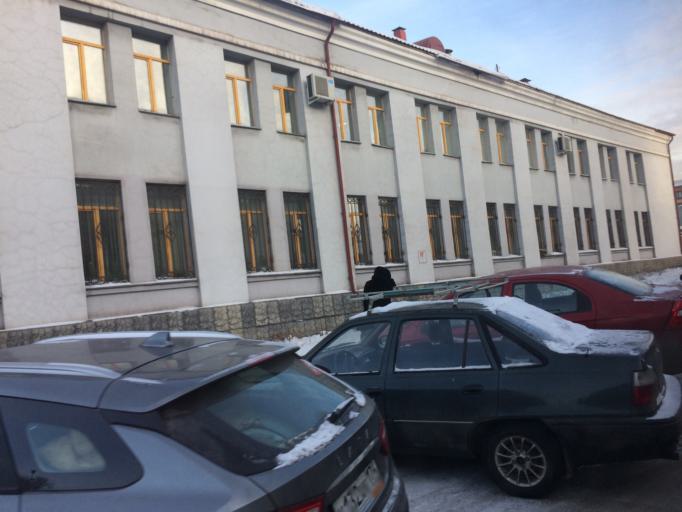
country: RU
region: Chelyabinsk
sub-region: Gorod Magnitogorsk
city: Magnitogorsk
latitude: 53.4117
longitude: 59.0572
